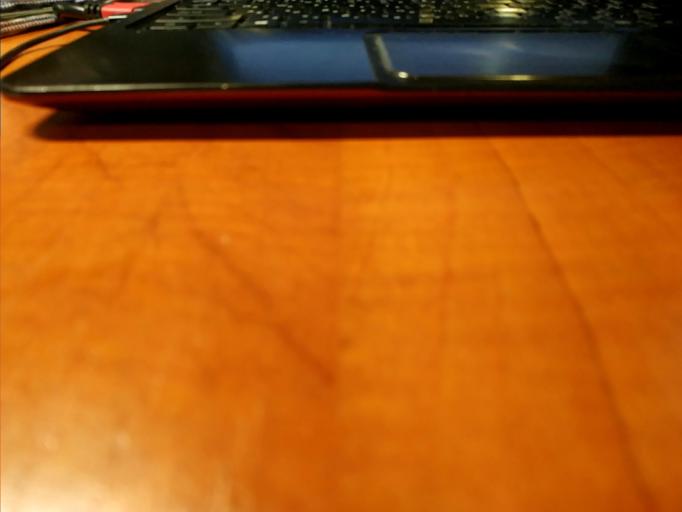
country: RU
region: Tverskaya
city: Ves'yegonsk
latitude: 58.7912
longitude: 37.5443
